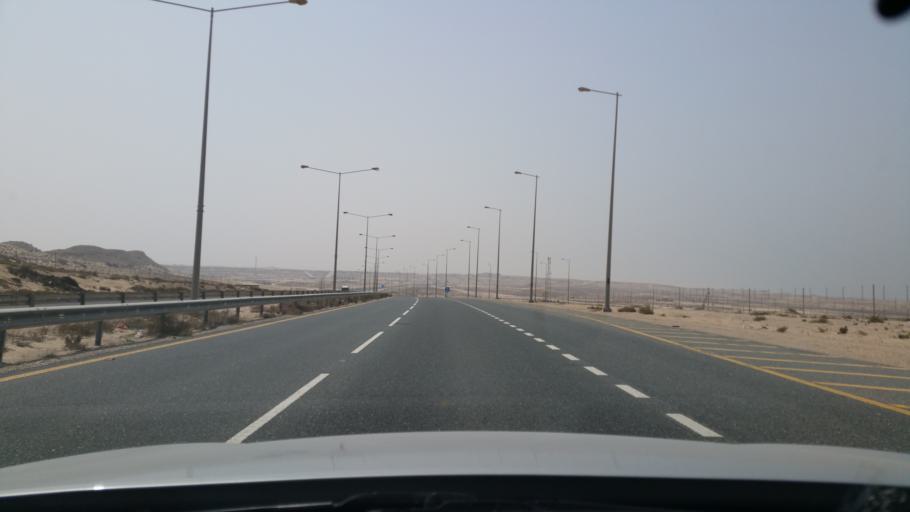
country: QA
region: Baladiyat ar Rayyan
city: Dukhan
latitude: 25.3553
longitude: 50.7795
